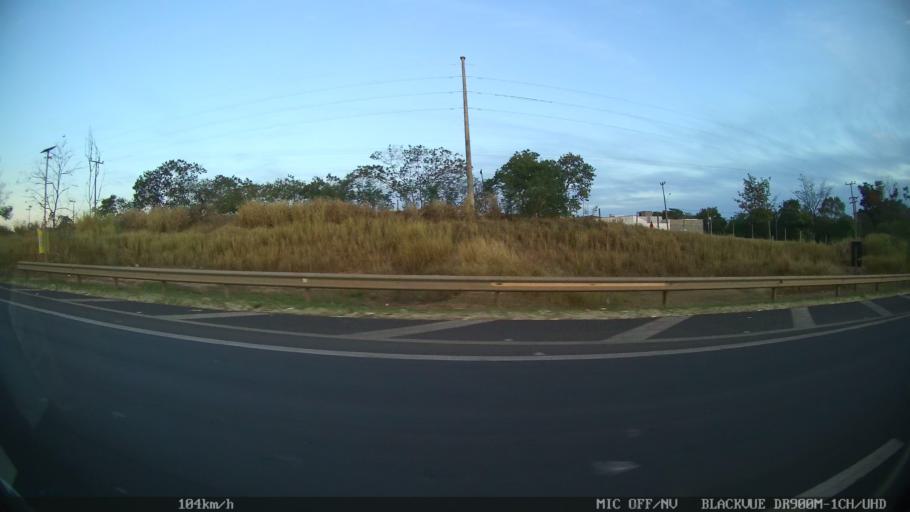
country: BR
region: Sao Paulo
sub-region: Catanduva
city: Catanduva
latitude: -21.1199
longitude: -48.9880
